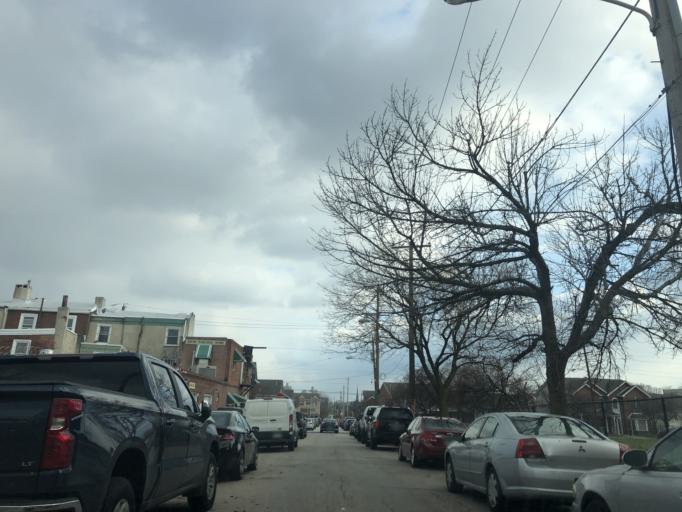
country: US
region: Pennsylvania
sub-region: Philadelphia County
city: Philadelphia
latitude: 39.9674
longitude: -75.1573
